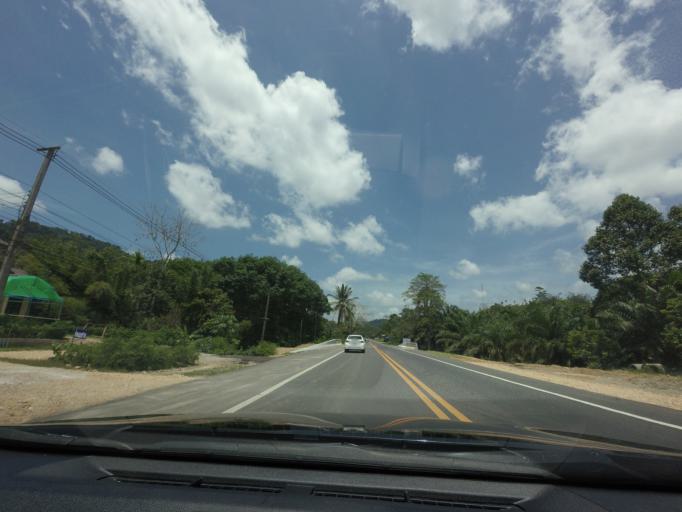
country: TH
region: Chumphon
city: Ban Nam Yuen
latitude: 9.9109
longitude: 98.9206
